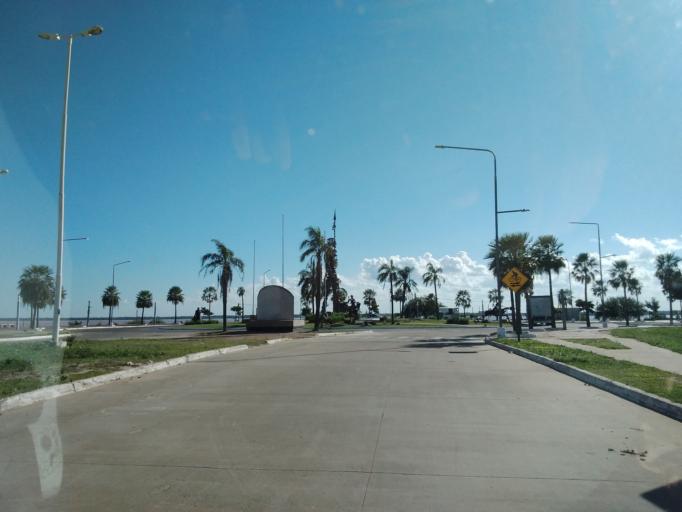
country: AR
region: Corrientes
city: Corrientes
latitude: -27.4812
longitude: -58.8536
